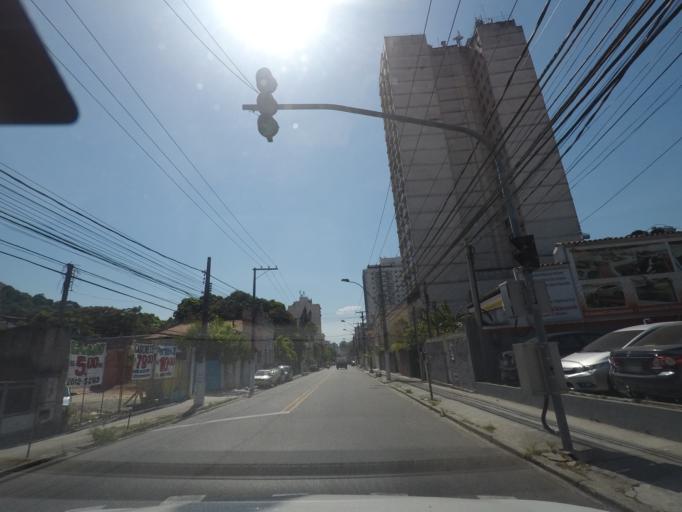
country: BR
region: Rio de Janeiro
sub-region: Niteroi
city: Niteroi
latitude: -22.9057
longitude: -43.0872
